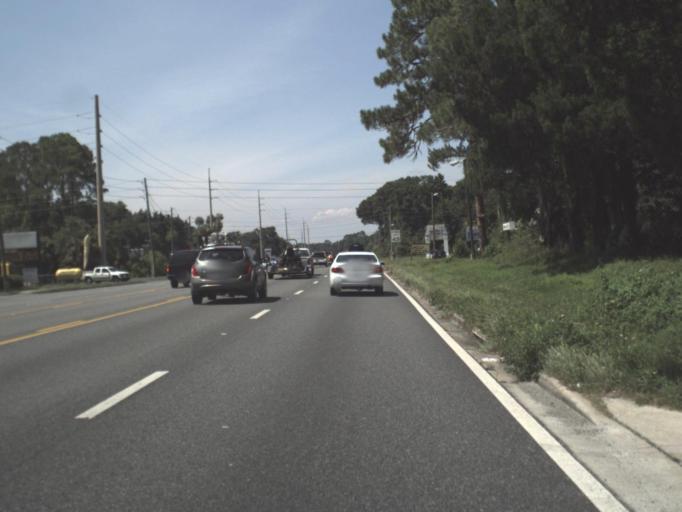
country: US
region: Florida
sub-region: Citrus County
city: Homosassa Springs
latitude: 28.8072
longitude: -82.5763
